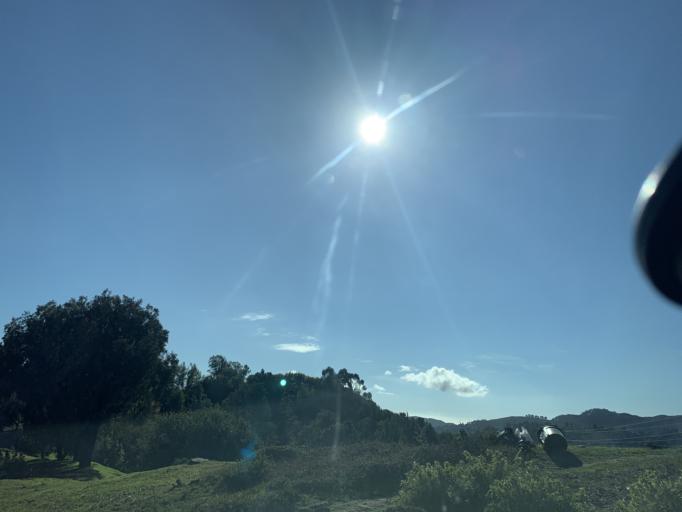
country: US
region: California
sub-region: Marin County
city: Strawberry
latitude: 37.9005
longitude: -122.5196
